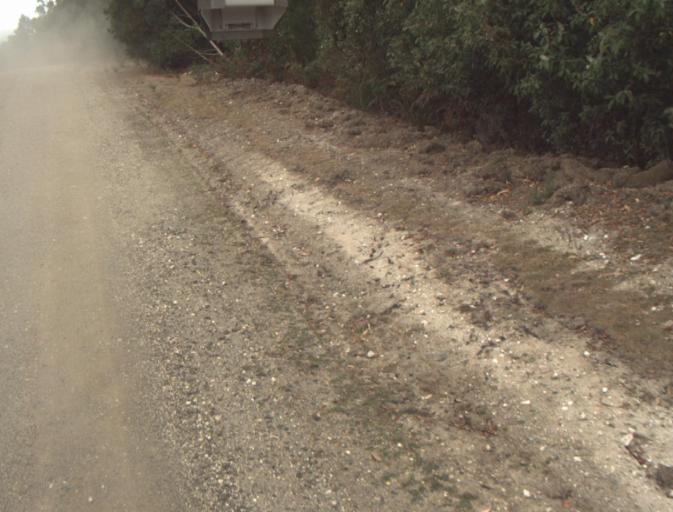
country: AU
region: Tasmania
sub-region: Launceston
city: Mayfield
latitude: -41.1633
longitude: 147.1777
